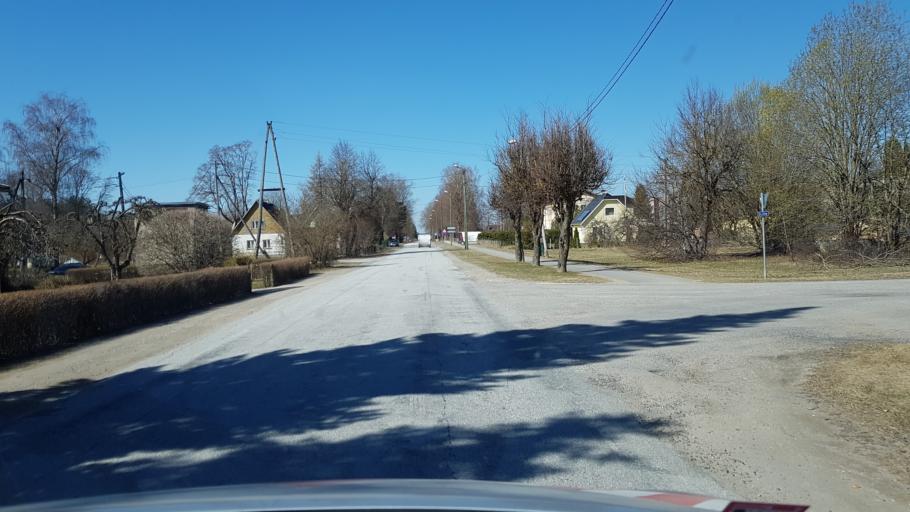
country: EE
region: Laeaene-Virumaa
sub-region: Rakke vald
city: Rakke
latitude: 58.9903
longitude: 26.2340
